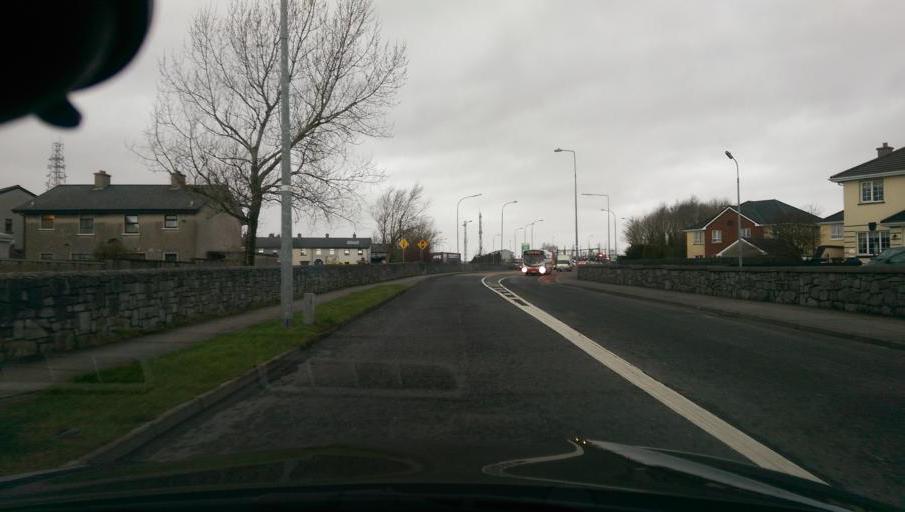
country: IE
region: Connaught
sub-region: County Galway
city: Gaillimh
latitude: 53.2866
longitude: -9.0120
